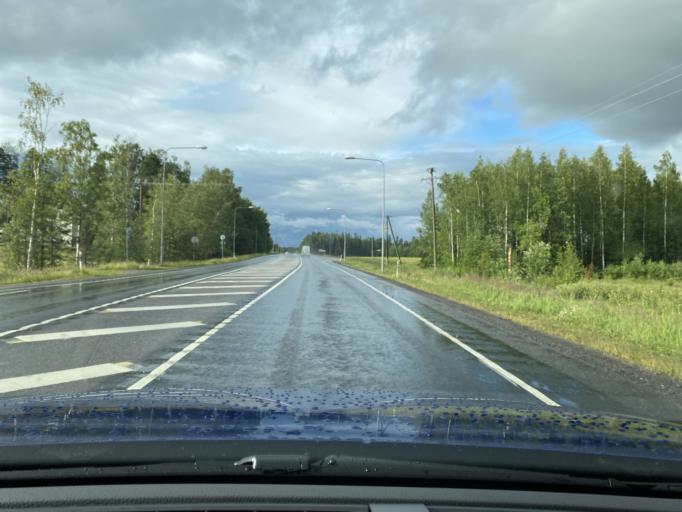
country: FI
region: Uusimaa
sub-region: Helsinki
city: Nurmijaervi
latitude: 60.4705
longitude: 24.8398
